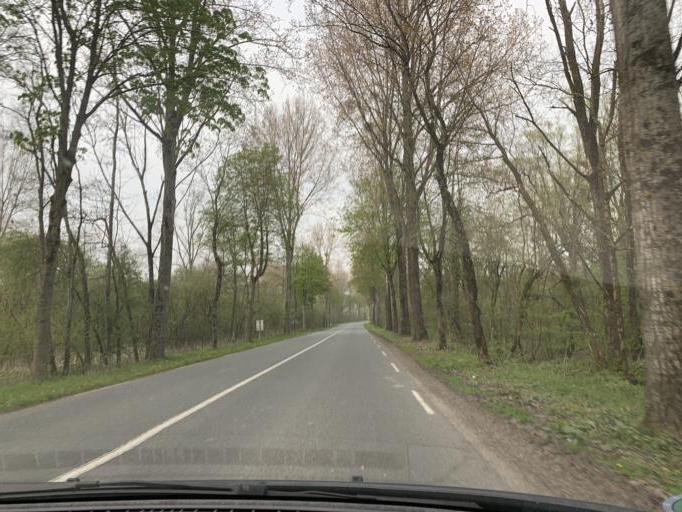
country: FR
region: Nord-Pas-de-Calais
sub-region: Departement du Pas-de-Calais
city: Montreuil
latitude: 50.4792
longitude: 1.7693
